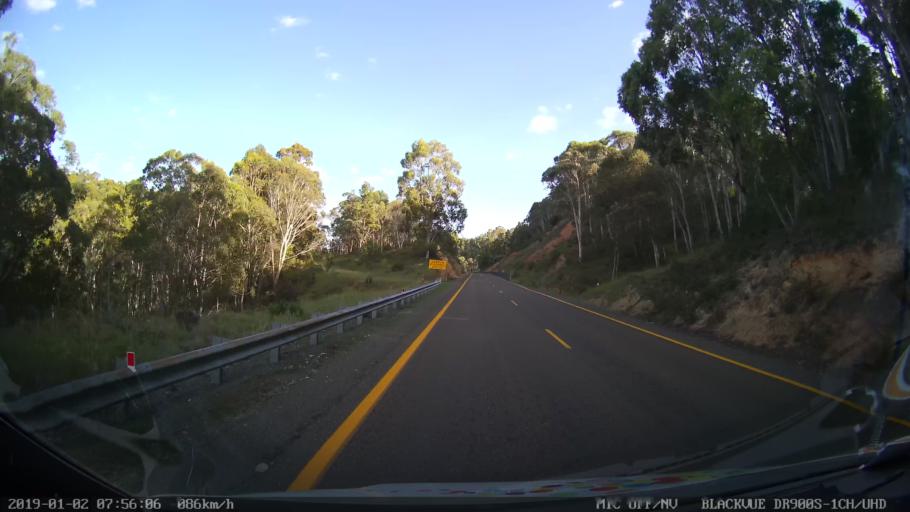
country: AU
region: New South Wales
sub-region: Tumut Shire
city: Tumut
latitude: -35.6748
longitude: 148.4860
